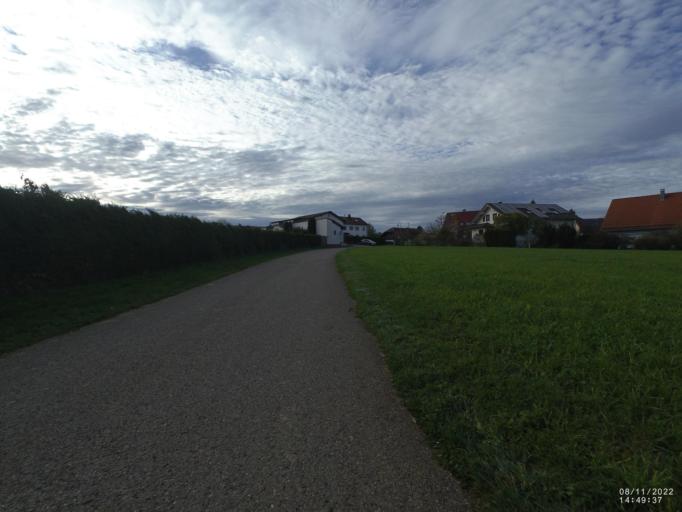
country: DE
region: Baden-Wuerttemberg
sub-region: Regierungsbezirk Stuttgart
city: Bad Uberkingen
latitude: 48.5821
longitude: 9.8056
